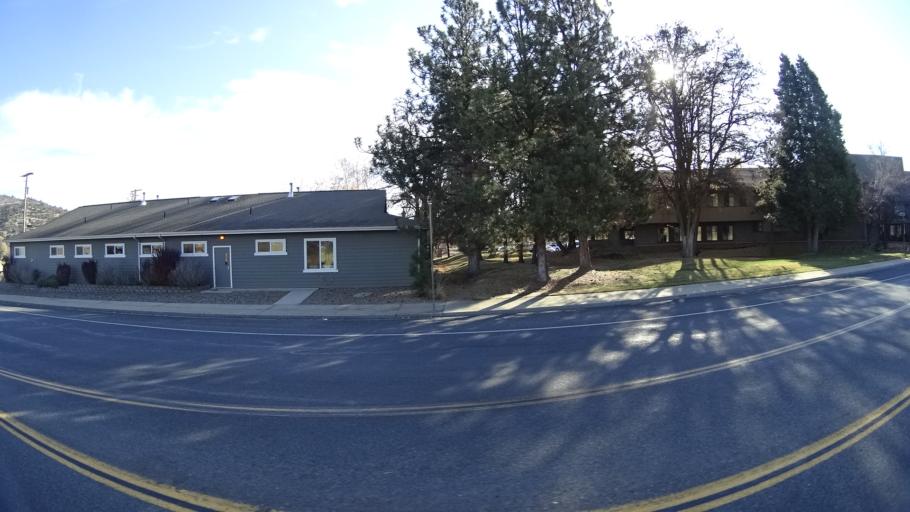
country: US
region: California
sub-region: Siskiyou County
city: Yreka
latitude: 41.7155
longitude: -122.6391
